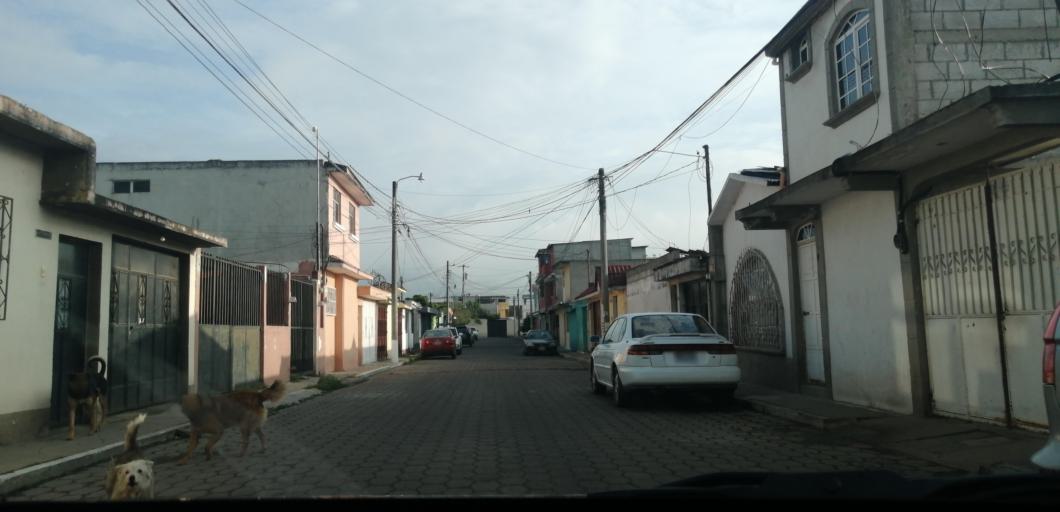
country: GT
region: Quetzaltenango
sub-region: Municipio de La Esperanza
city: La Esperanza
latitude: 14.8647
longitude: -91.5442
